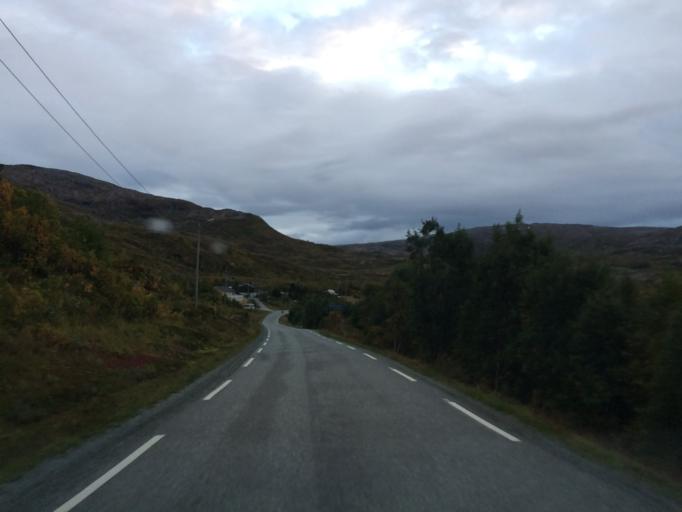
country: NO
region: Troms
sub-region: Lenvik
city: Finnsnes
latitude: 69.6247
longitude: 18.2228
